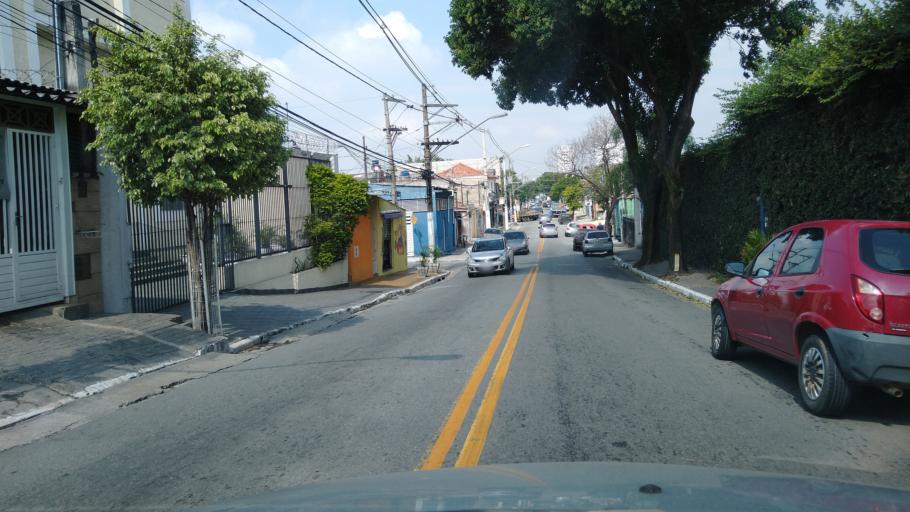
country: BR
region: Sao Paulo
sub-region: Guarulhos
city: Guarulhos
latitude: -23.4722
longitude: -46.5765
